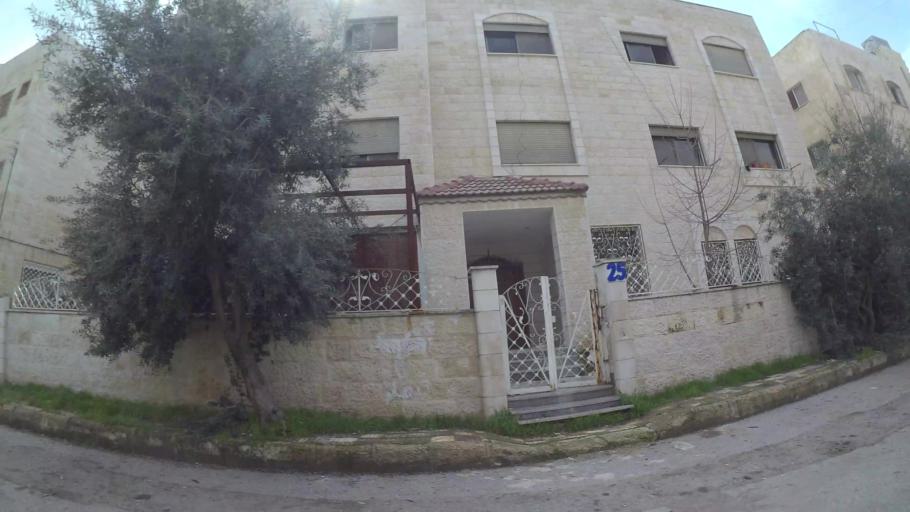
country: JO
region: Amman
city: Umm as Summaq
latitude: 31.8980
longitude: 35.8383
